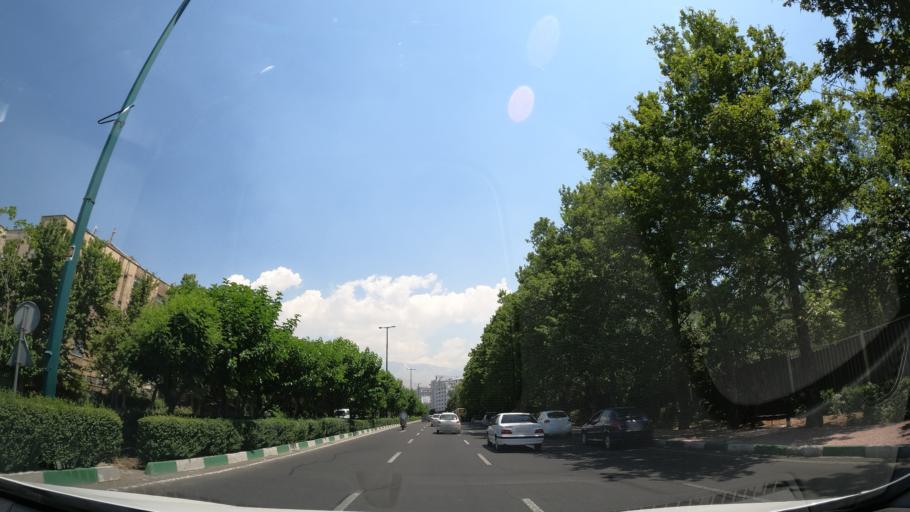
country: IR
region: Tehran
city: Tajrish
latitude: 35.7645
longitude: 51.3774
